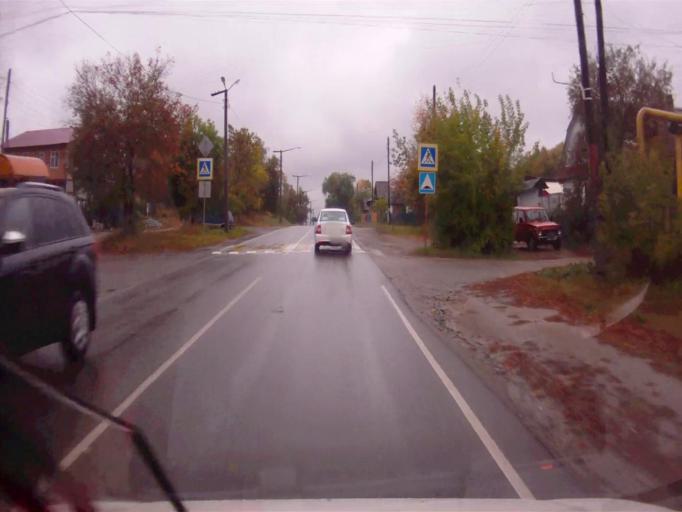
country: RU
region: Chelyabinsk
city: Kyshtym
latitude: 55.7219
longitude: 60.5330
